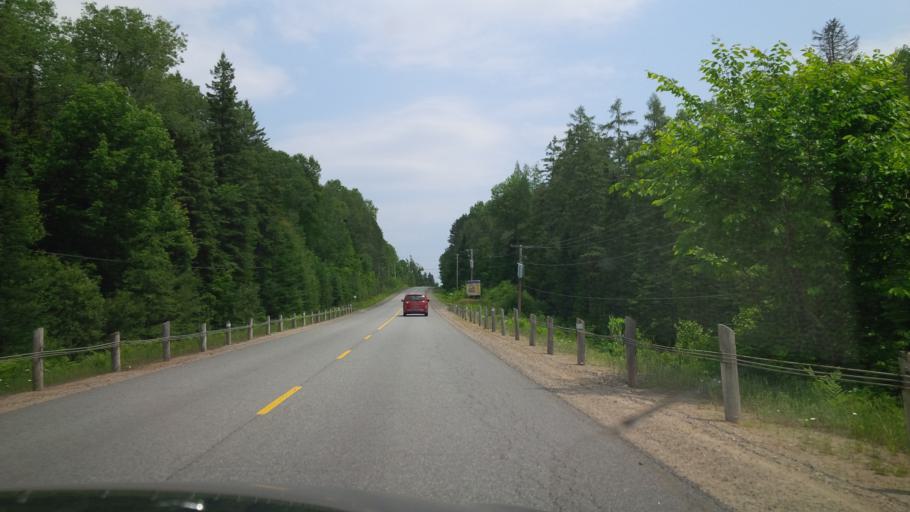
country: CA
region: Ontario
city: Huntsville
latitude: 45.5494
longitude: -79.2419
